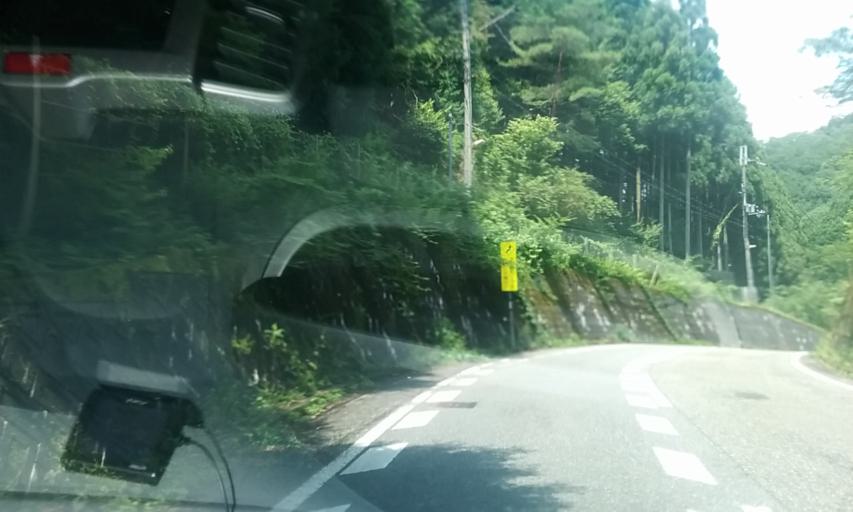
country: JP
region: Hyogo
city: Sasayama
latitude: 35.1741
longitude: 135.2469
